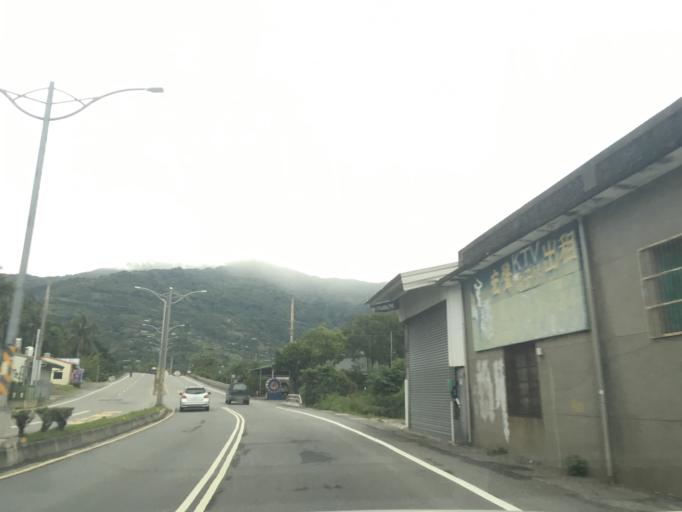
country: TW
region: Taiwan
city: Taitung City
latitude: 22.6987
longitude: 121.0420
